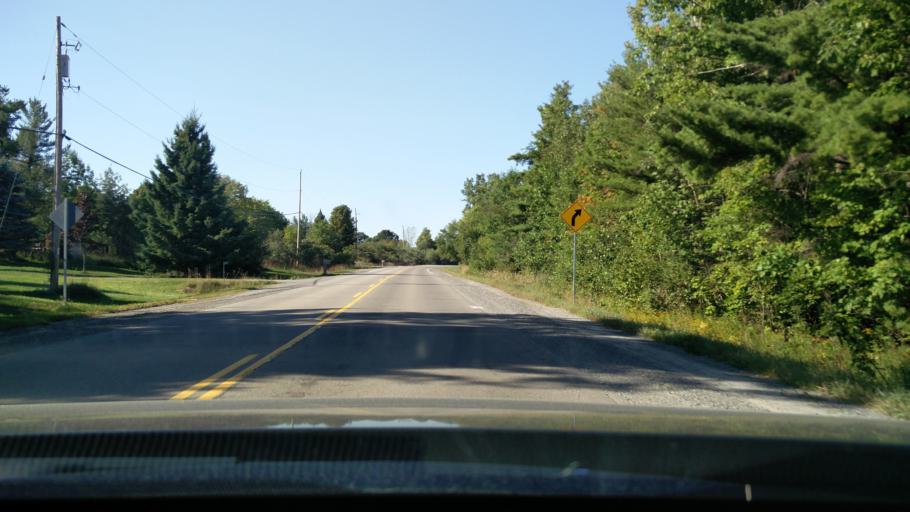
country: CA
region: Ontario
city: Perth
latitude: 44.6920
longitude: -76.3999
